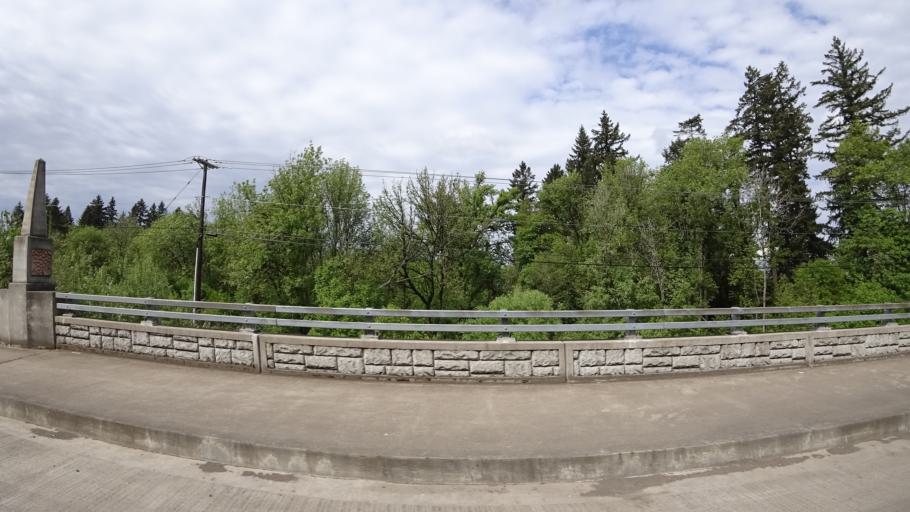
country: US
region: Oregon
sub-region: Washington County
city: Hillsboro
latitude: 45.4978
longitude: -122.9496
